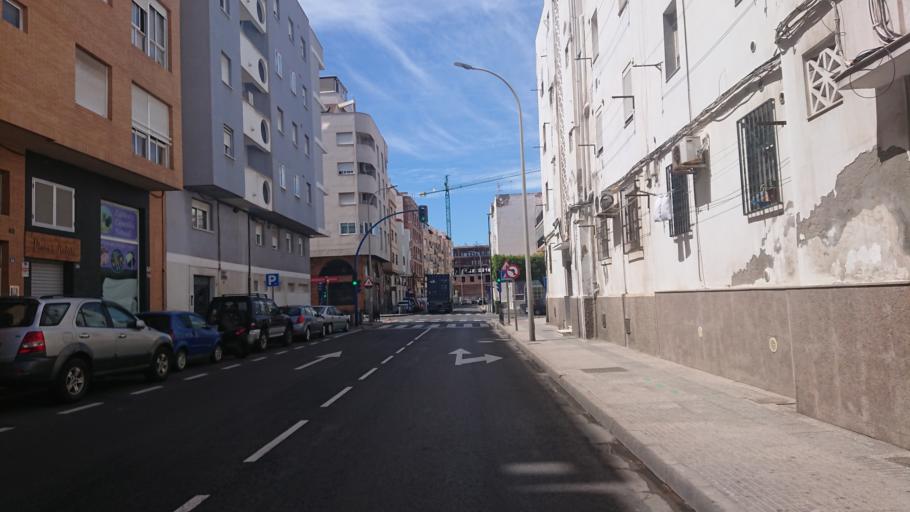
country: ES
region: Melilla
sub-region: Melilla
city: Melilla
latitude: 35.2807
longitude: -2.9399
